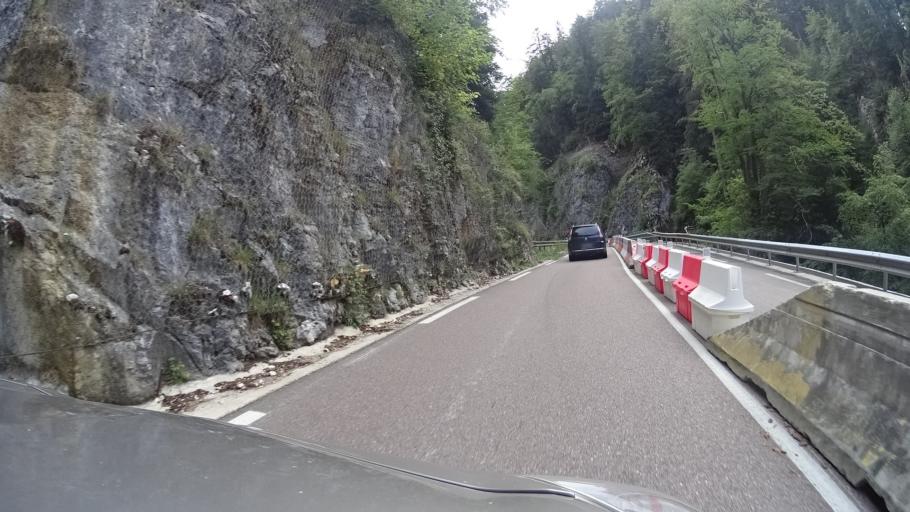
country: FR
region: Franche-Comte
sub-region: Departement du Jura
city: Champagnole
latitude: 46.6667
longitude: 5.9457
